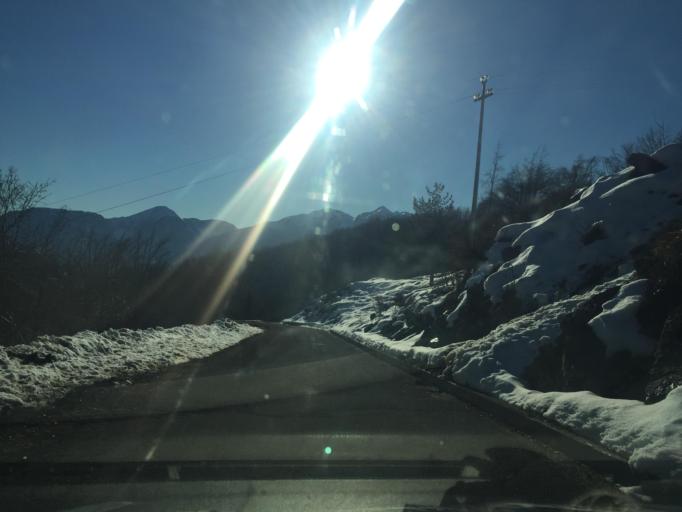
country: IT
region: Friuli Venezia Giulia
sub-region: Provincia di Udine
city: Lauco
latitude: 46.4404
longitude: 12.9635
